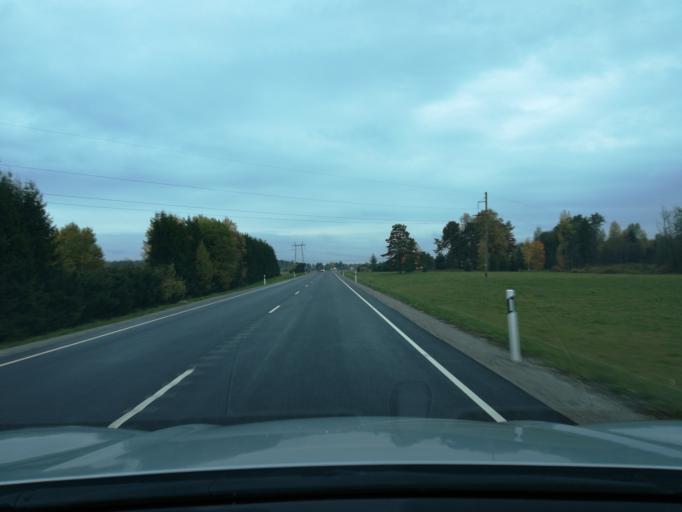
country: EE
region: Ida-Virumaa
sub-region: Johvi vald
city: Johvi
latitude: 59.0789
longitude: 27.3156
